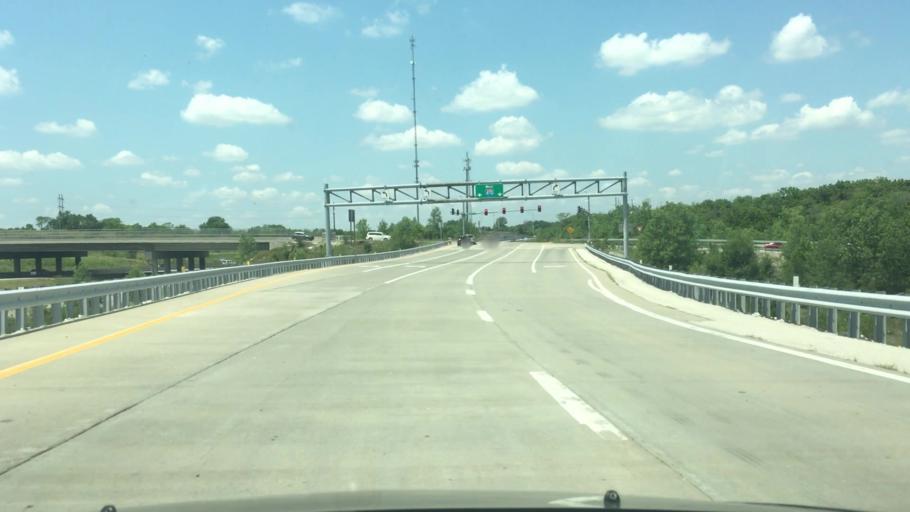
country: US
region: Missouri
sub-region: Jackson County
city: Lees Summit
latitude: 38.9351
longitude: -94.4103
